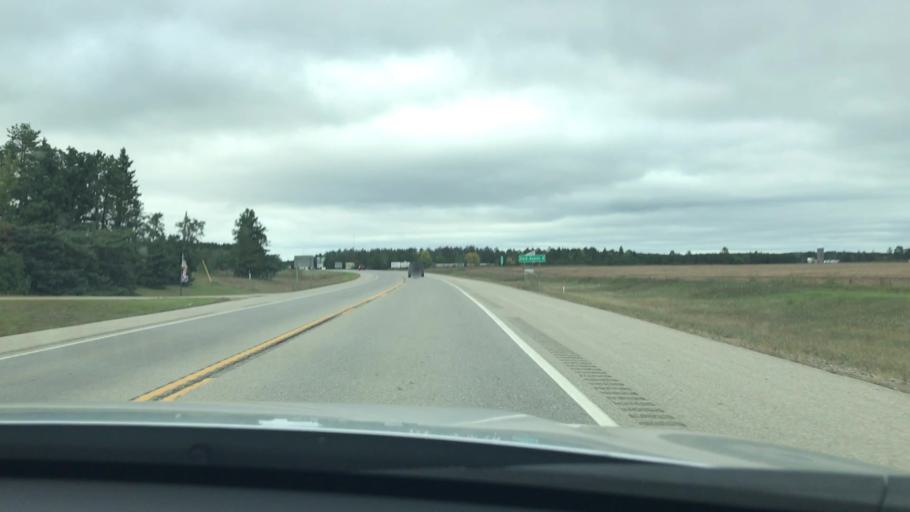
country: US
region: Minnesota
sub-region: Hubbard County
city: Park Rapids
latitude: 46.8655
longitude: -95.0690
